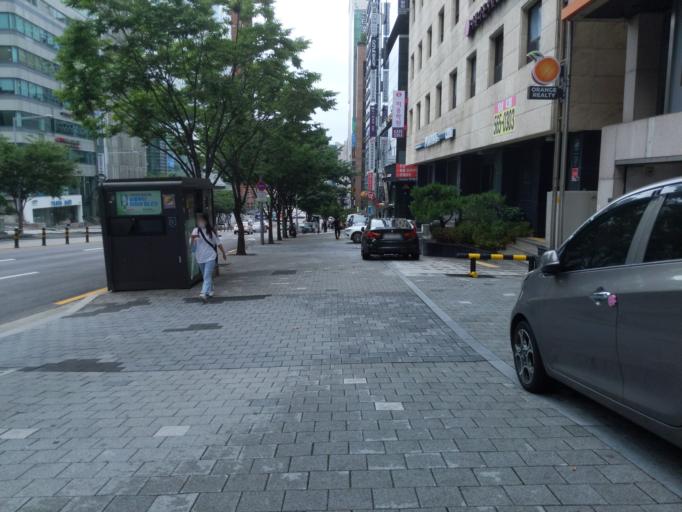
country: KR
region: Seoul
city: Seoul
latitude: 37.5053
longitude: 127.0268
